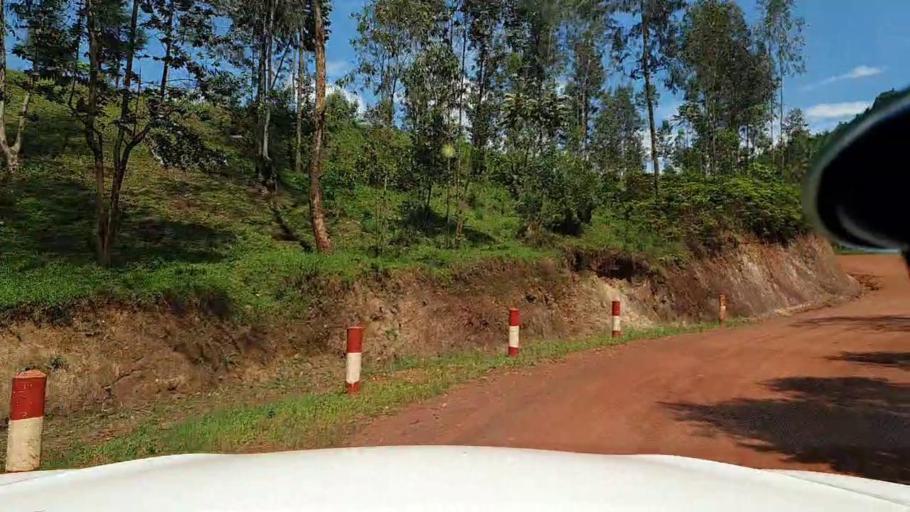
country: RW
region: Kigali
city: Kigali
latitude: -1.7610
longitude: 29.8709
